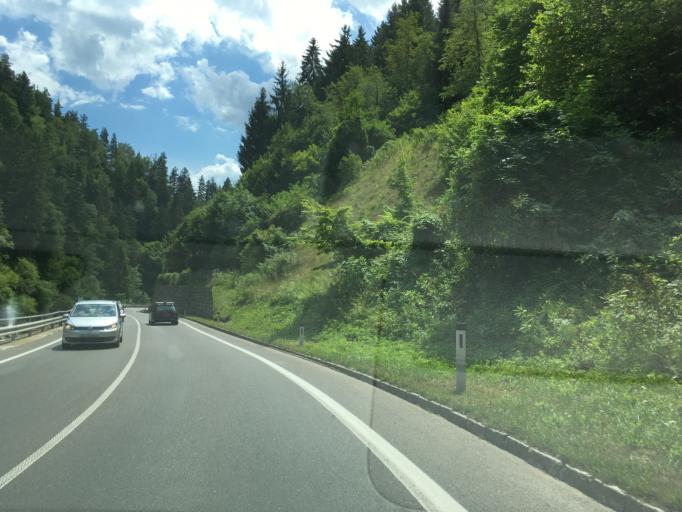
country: AT
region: Carinthia
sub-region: Politischer Bezirk Spittal an der Drau
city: Spittal an der Drau
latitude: 46.8134
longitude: 13.4901
